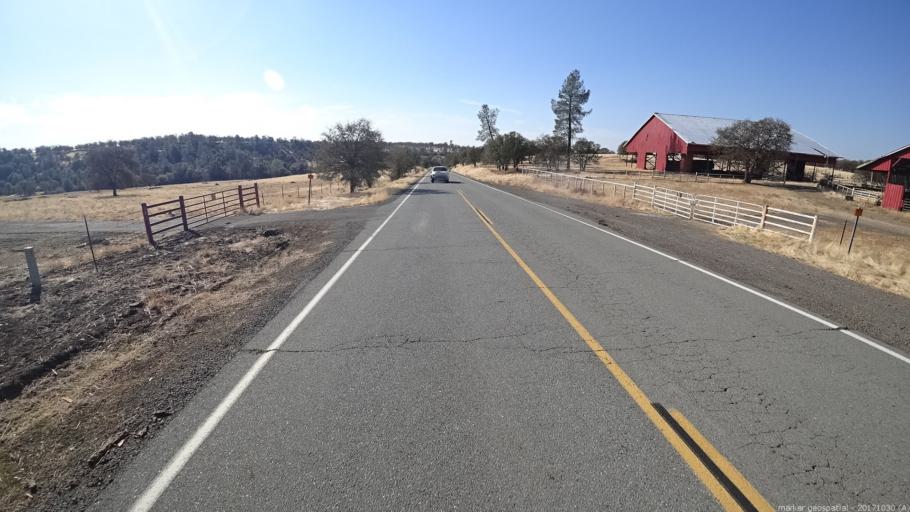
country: US
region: California
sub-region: Shasta County
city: Bella Vista
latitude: 40.6735
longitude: -122.0556
